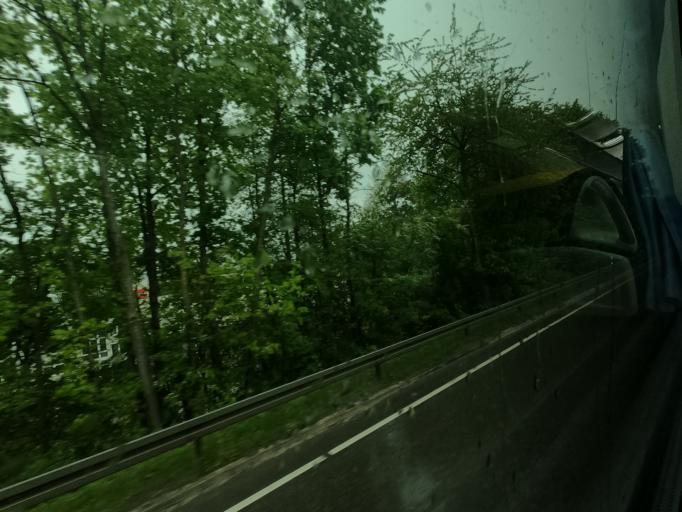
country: DE
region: Baden-Wuerttemberg
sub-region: Regierungsbezirk Stuttgart
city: Aalen
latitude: 48.8297
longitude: 10.0994
